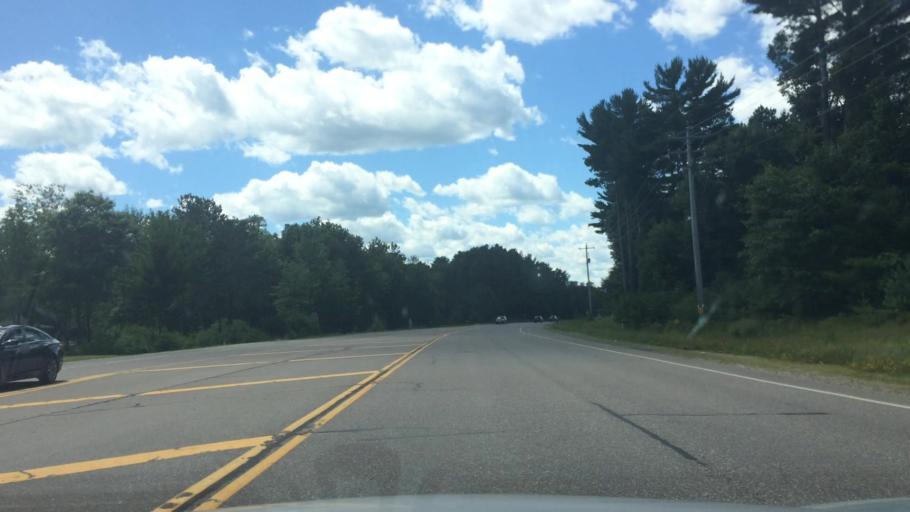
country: US
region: Wisconsin
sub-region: Vilas County
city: Lac du Flambeau
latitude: 45.8838
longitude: -89.7339
